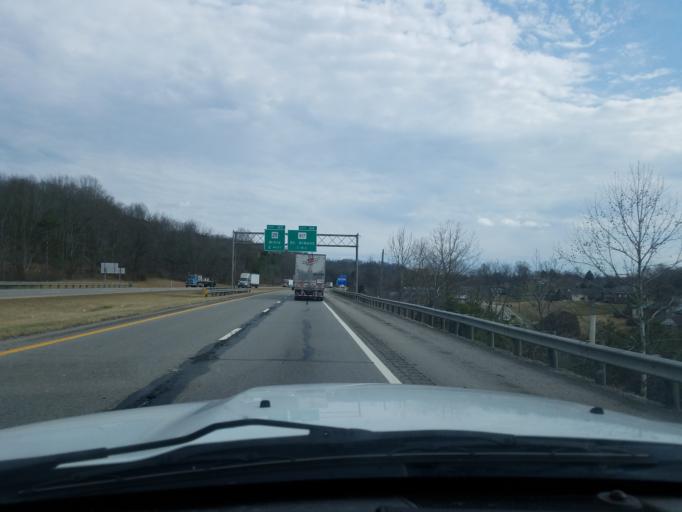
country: US
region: West Virginia
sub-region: Kanawha County
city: Nitro
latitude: 38.4543
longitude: -81.8675
